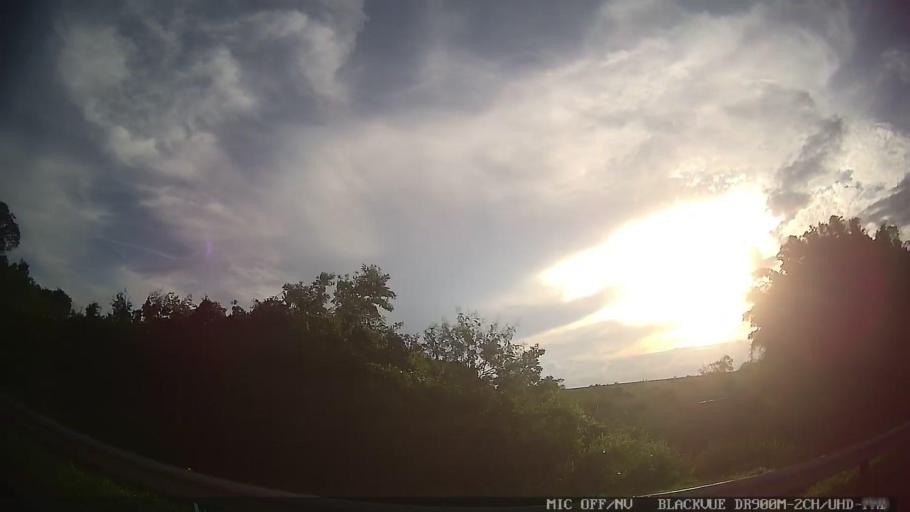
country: BR
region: Sao Paulo
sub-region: Tiete
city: Tiete
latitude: -23.1484
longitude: -47.6668
